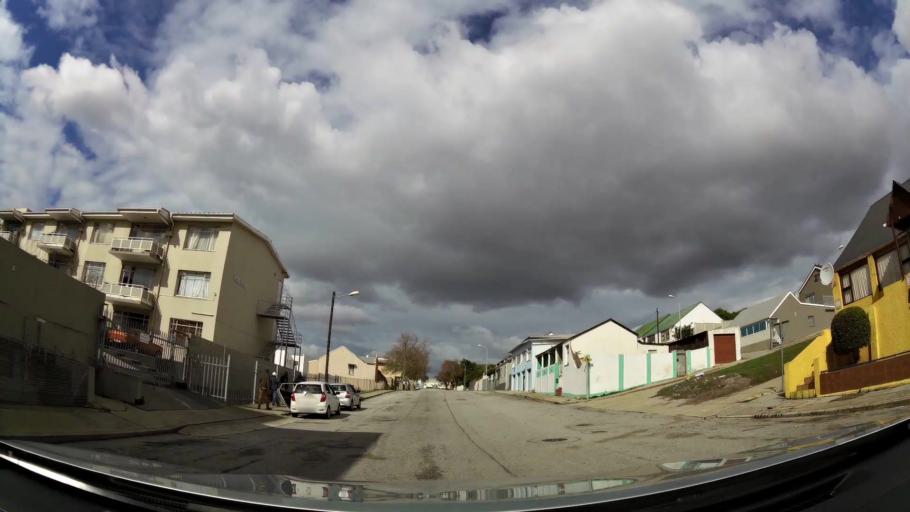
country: ZA
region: Eastern Cape
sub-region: Nelson Mandela Bay Metropolitan Municipality
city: Port Elizabeth
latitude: -33.9517
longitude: 25.6069
